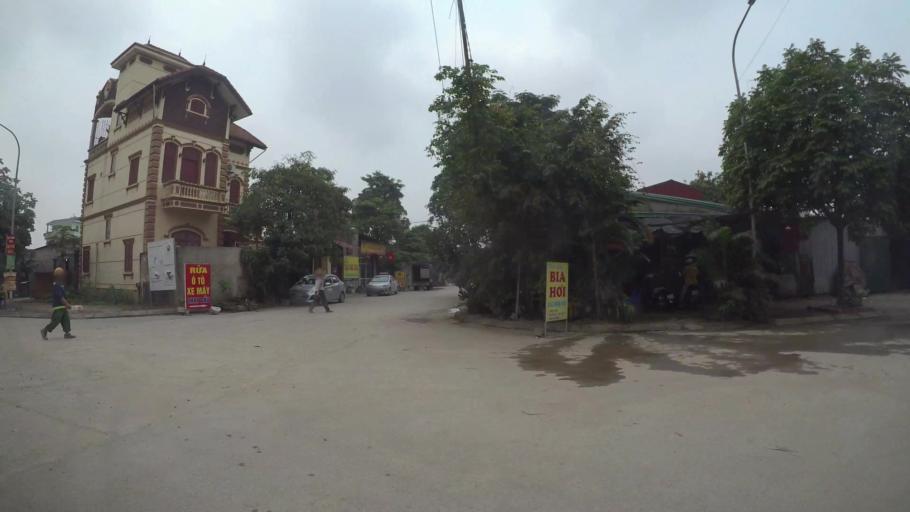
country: VN
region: Ha Noi
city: Ha Dong
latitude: 20.9866
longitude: 105.7512
